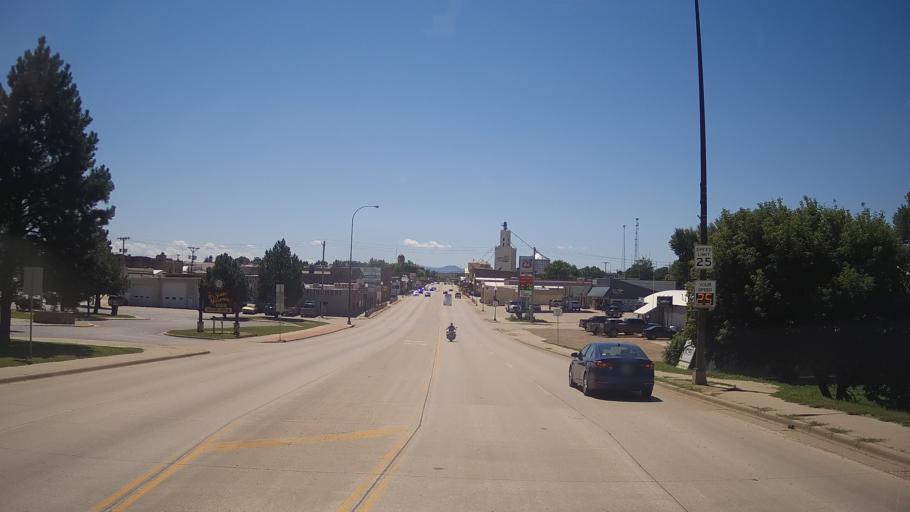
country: US
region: South Dakota
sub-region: Butte County
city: Belle Fourche
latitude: 44.6745
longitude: -103.8536
